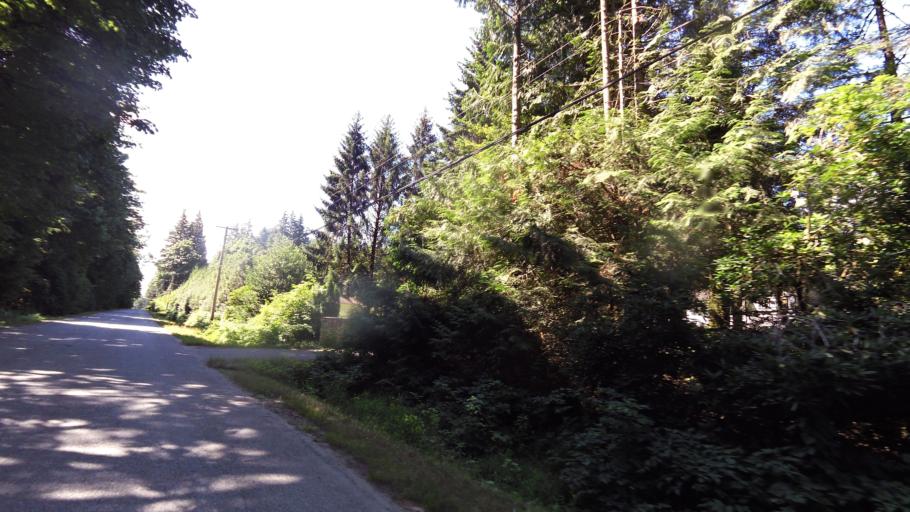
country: CA
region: British Columbia
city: Aldergrove
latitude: 49.2297
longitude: -122.3691
